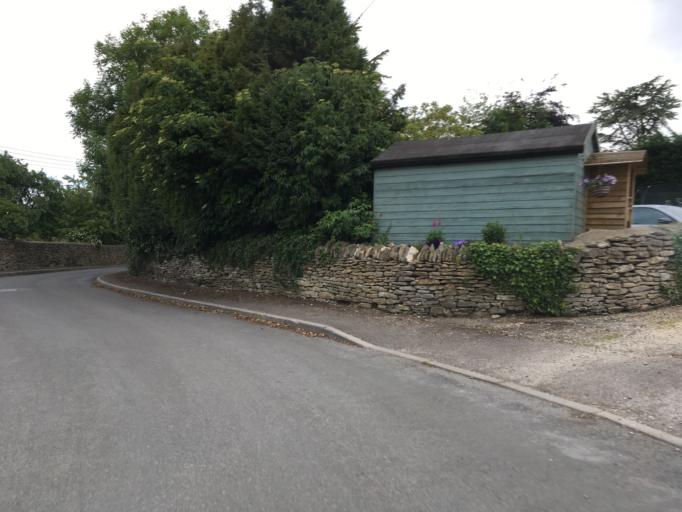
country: GB
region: England
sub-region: South Gloucestershire
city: Horton
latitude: 51.5827
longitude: -2.3175
